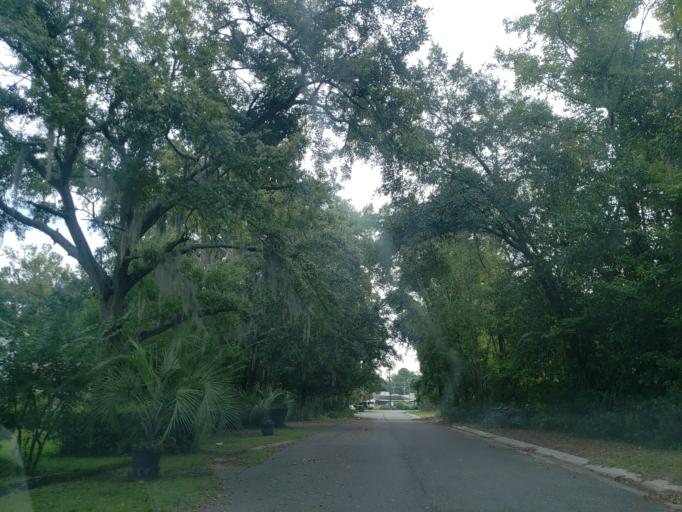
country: US
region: Georgia
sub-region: Chatham County
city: Isle of Hope
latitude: 31.9857
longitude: -81.0760
